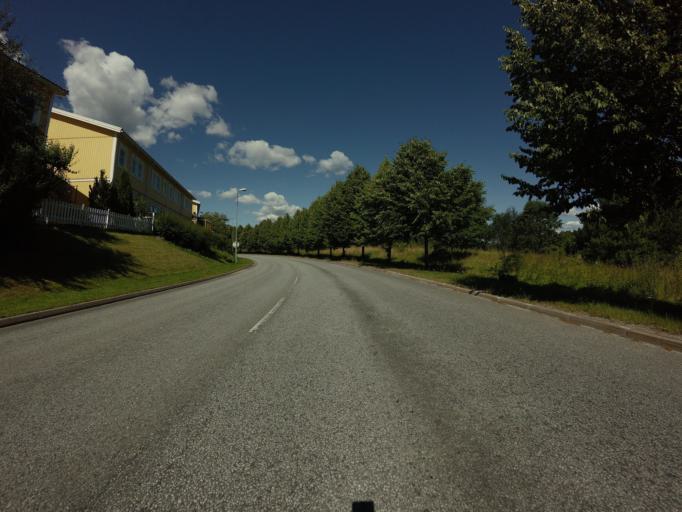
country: SE
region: Stockholm
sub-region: Upplands Vasby Kommun
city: Upplands Vaesby
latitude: 59.4617
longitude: 17.8988
